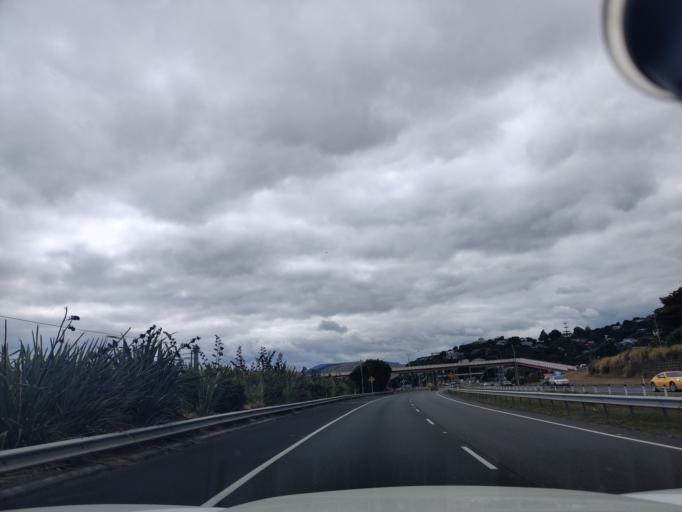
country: NZ
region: Wellington
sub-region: Porirua City
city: Porirua
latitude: -41.1083
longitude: 174.8626
